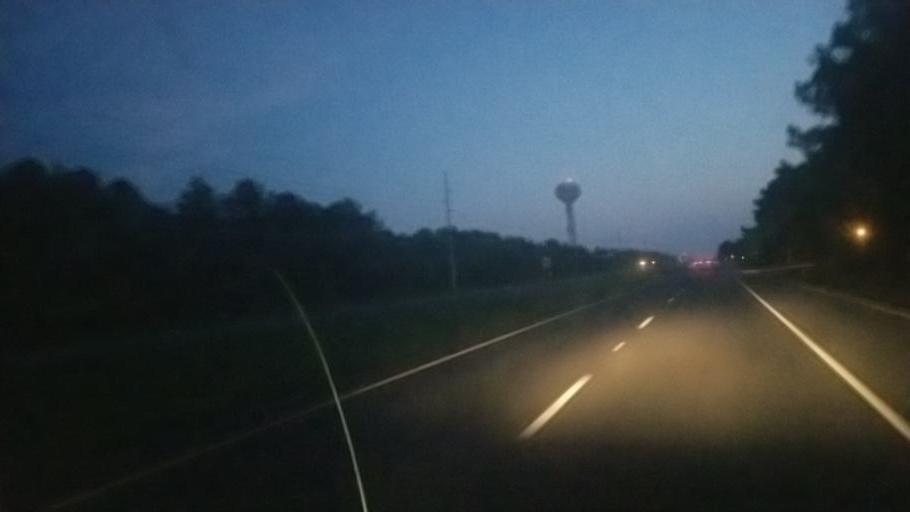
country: US
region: Delaware
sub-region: Sussex County
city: Bethany Beach
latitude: 38.5614
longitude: -75.0601
